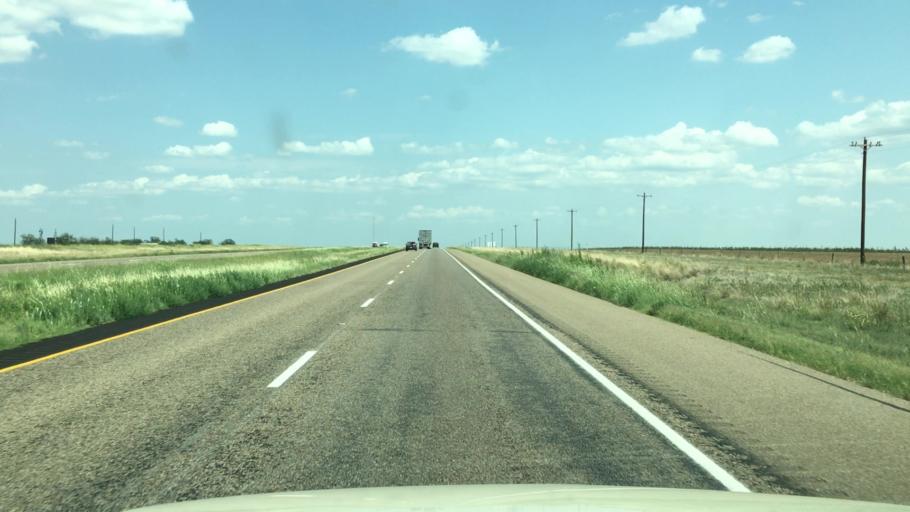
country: US
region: Texas
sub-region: Armstrong County
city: Claude
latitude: 35.0336
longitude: -101.1749
